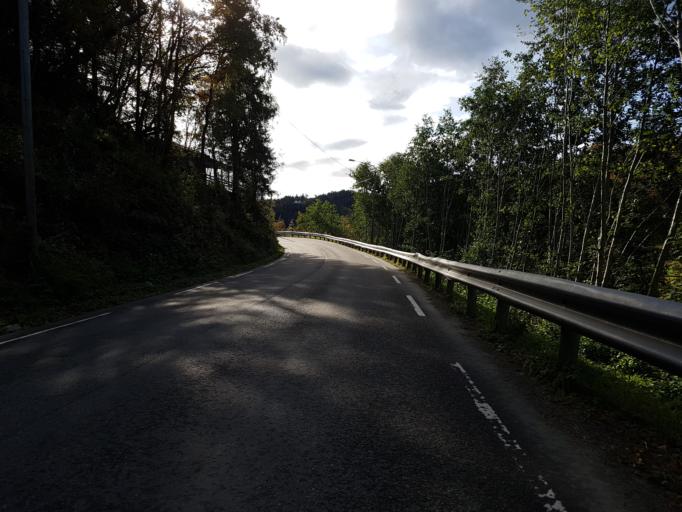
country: NO
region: Sor-Trondelag
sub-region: Klaebu
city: Klaebu
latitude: 63.3988
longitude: 10.5242
